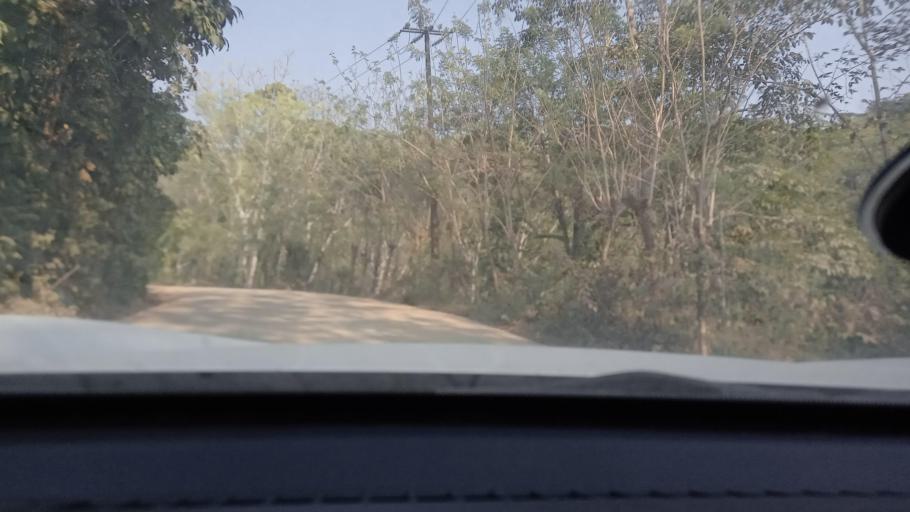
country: MX
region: Tabasco
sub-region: Huimanguillo
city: Francisco Rueda
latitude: 17.6557
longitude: -93.8751
